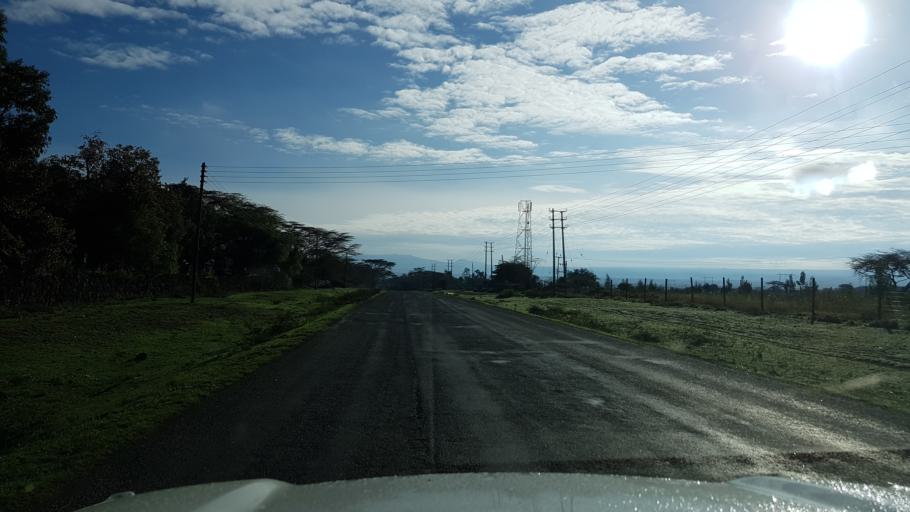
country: KE
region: Nakuru
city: Naivasha
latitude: -0.8170
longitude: 36.3936
